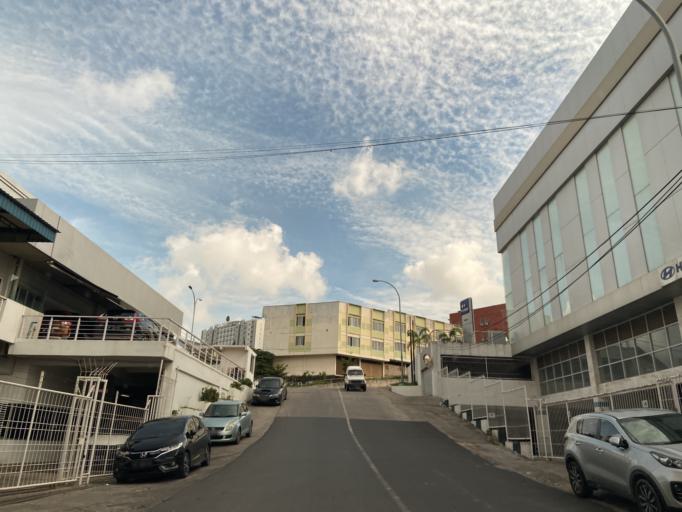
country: SG
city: Singapore
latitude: 1.1414
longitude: 104.0175
